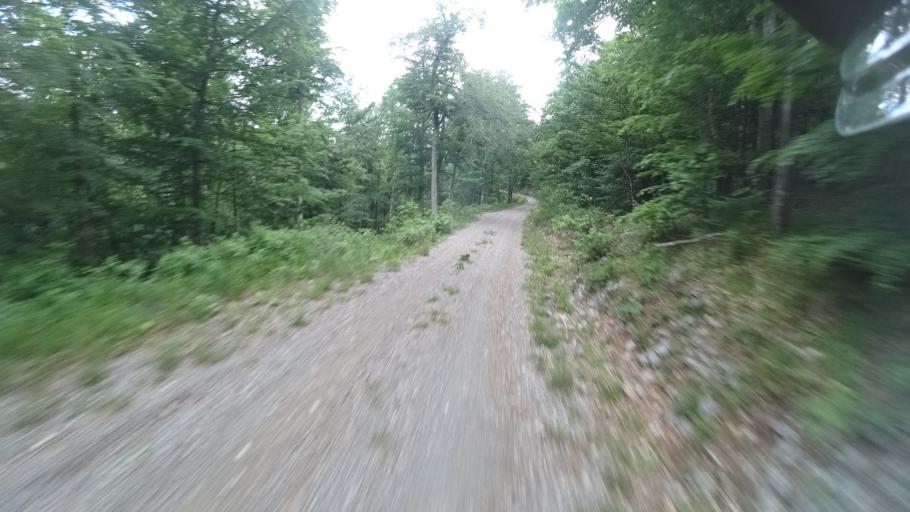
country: HR
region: Licko-Senjska
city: Gospic
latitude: 44.4468
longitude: 15.3028
